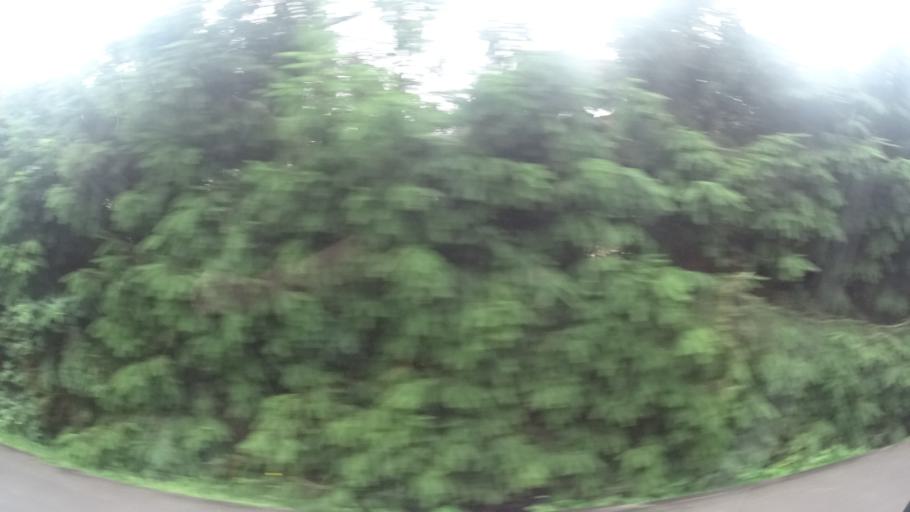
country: DE
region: Hesse
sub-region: Regierungsbezirk Darmstadt
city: Bad Soden-Salmunster
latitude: 50.2722
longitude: 9.3776
